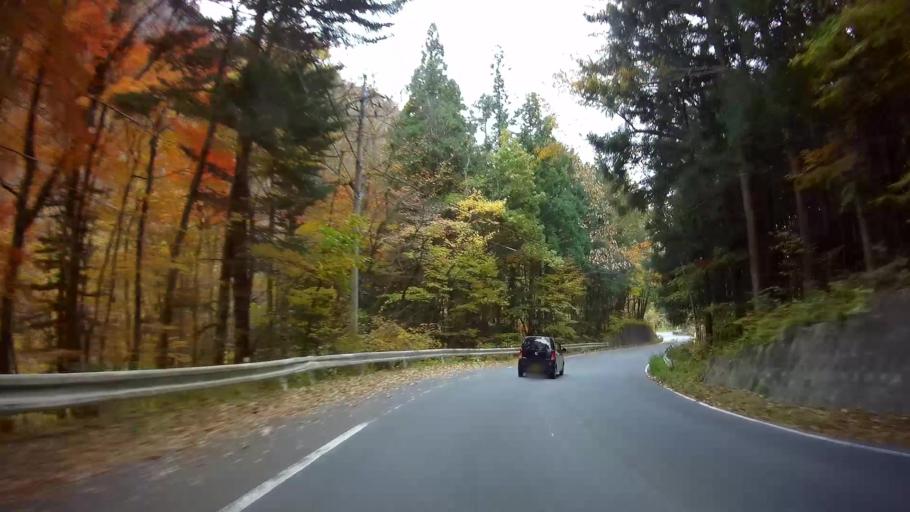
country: JP
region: Gunma
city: Nakanojomachi
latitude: 36.6198
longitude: 138.6451
